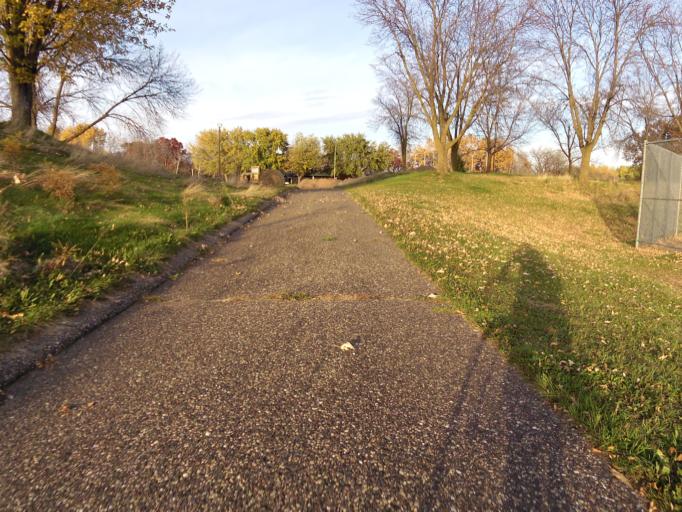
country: US
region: Minnesota
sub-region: Washington County
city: Lake Elmo
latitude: 44.9716
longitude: -92.8808
